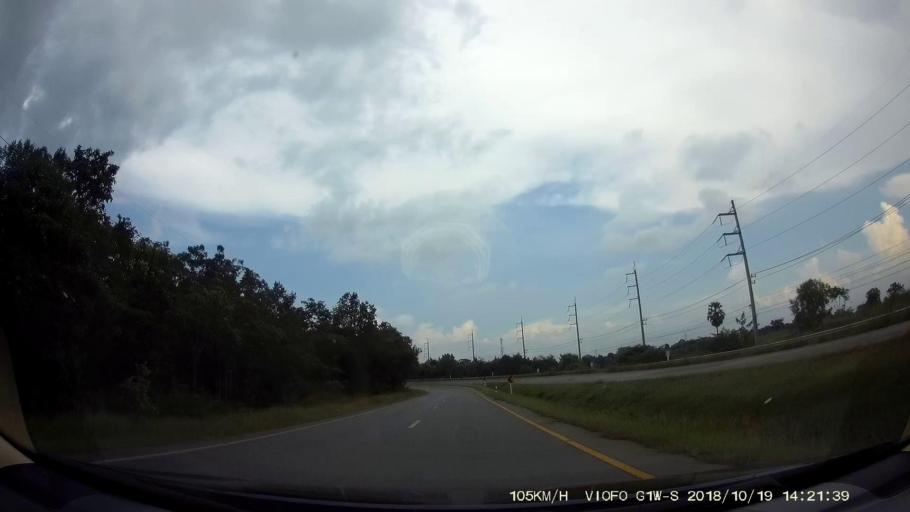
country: TH
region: Chaiyaphum
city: Kaeng Khro
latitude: 16.0543
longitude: 102.2691
